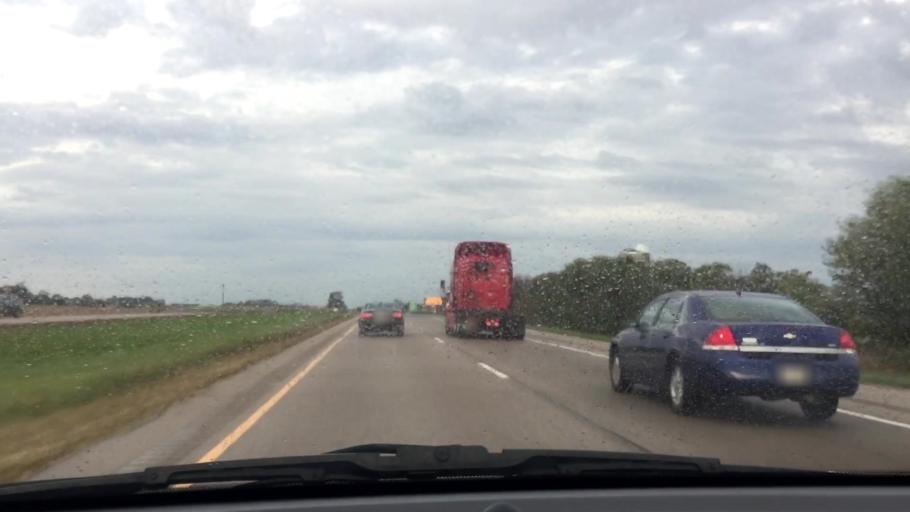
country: US
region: Wisconsin
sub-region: Rock County
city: Clinton
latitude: 42.5724
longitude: -88.8321
